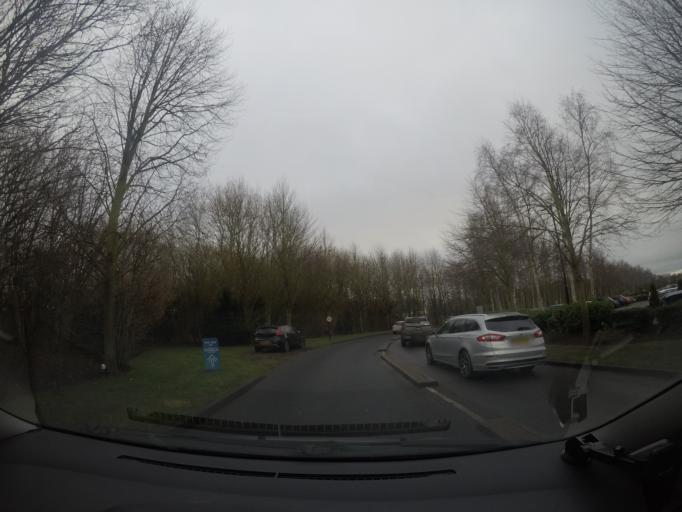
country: GB
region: England
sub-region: City of York
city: Fulford
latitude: 53.9219
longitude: -1.0732
